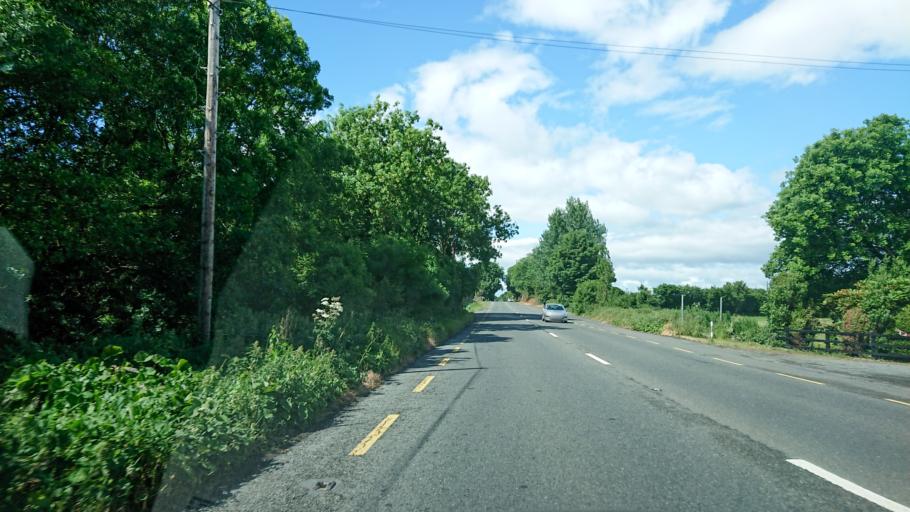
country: IE
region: Munster
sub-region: Waterford
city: Waterford
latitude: 52.2365
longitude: -7.1836
